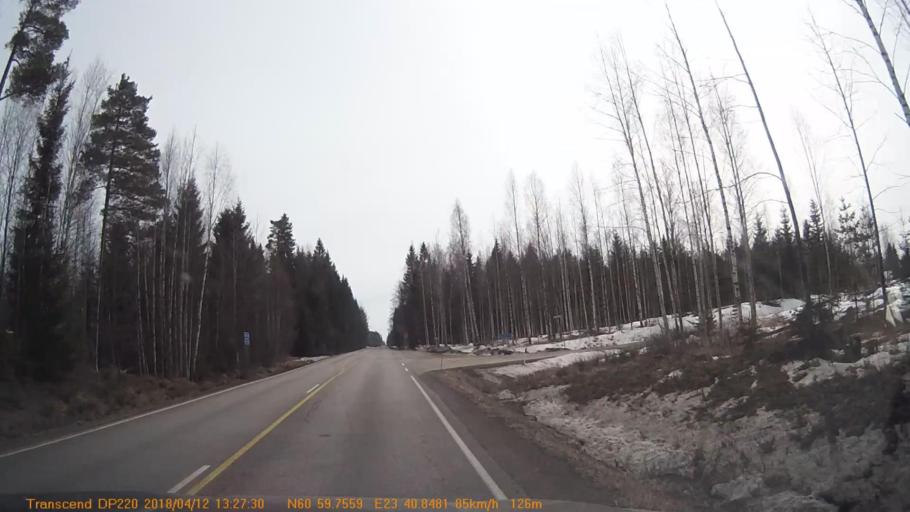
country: FI
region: Pirkanmaa
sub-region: Etelae-Pirkanmaa
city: Kylmaekoski
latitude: 60.9957
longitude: 23.6810
